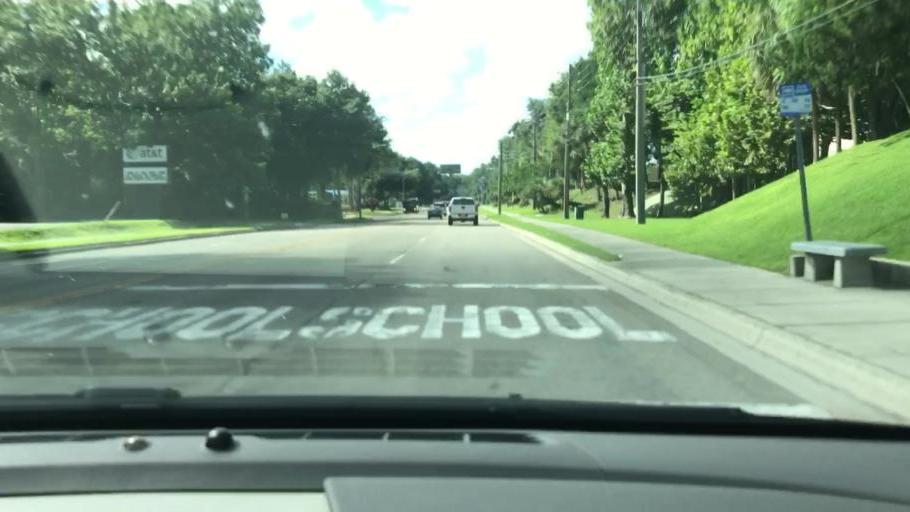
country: US
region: Florida
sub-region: Alachua County
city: Gainesville
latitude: 29.6569
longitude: -82.4089
